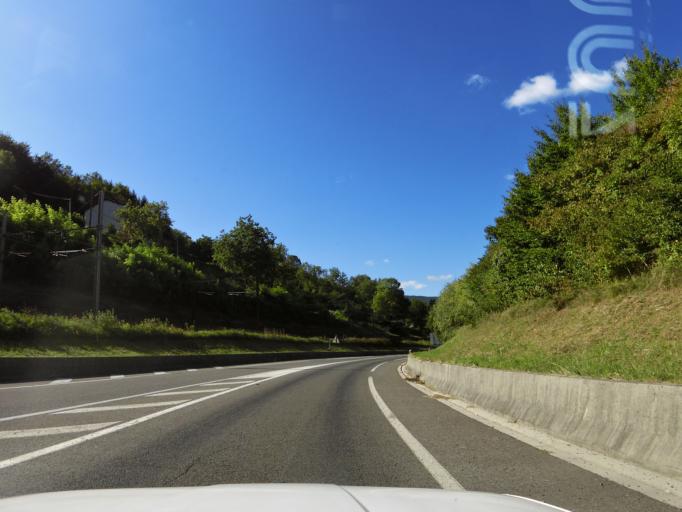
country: FR
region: Rhone-Alpes
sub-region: Departement de l'Ain
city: Tenay
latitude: 45.9321
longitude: 5.4891
